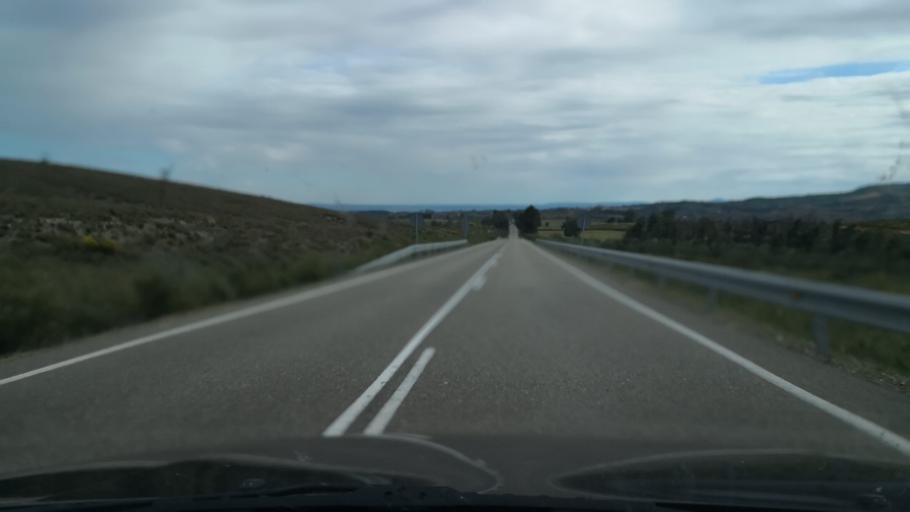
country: ES
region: Extremadura
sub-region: Provincia de Caceres
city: Acebo
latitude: 40.1967
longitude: -6.6761
